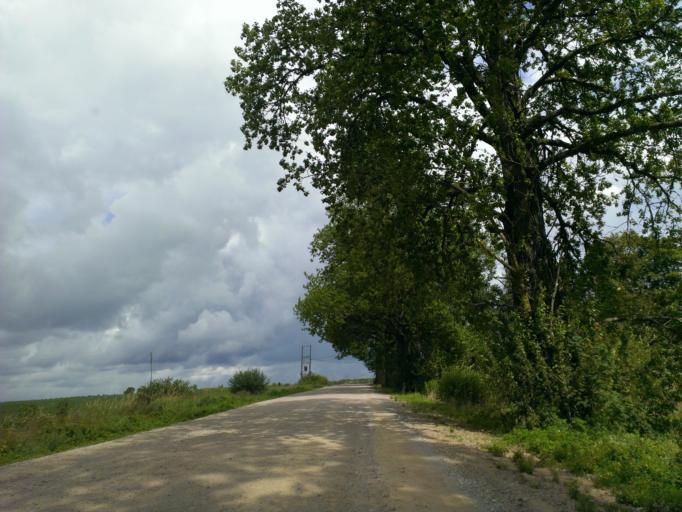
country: LV
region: Sigulda
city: Sigulda
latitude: 57.1773
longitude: 24.9246
